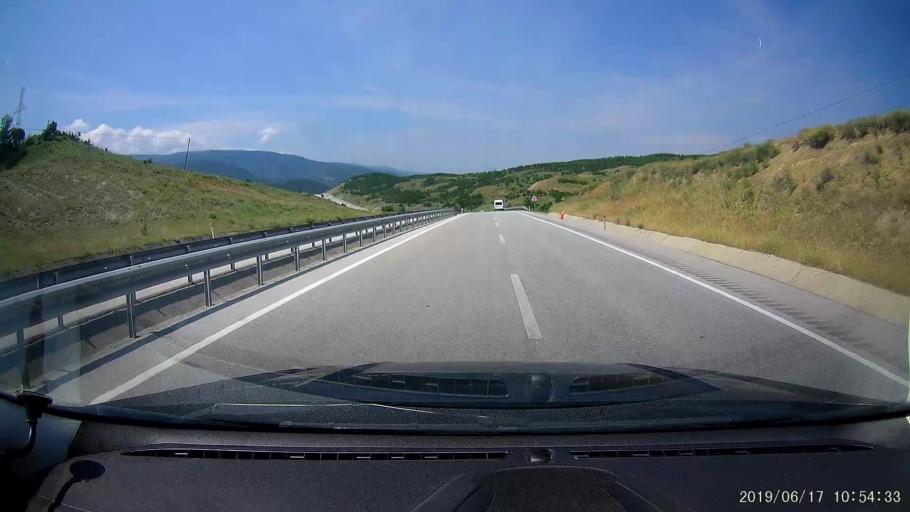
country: TR
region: Corum
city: Hacihamza
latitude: 41.0697
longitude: 34.2979
